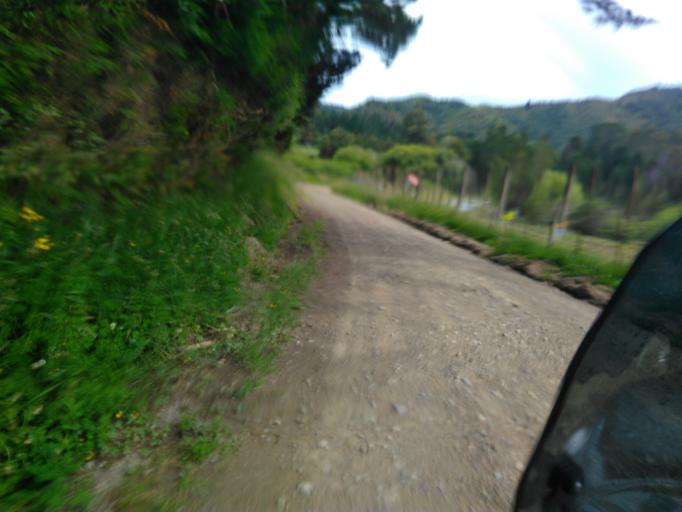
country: NZ
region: Bay of Plenty
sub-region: Opotiki District
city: Opotiki
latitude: -38.1107
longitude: 177.5076
